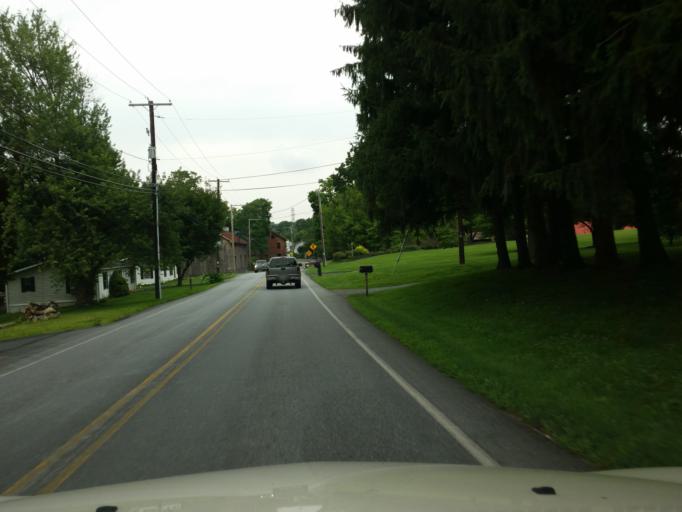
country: US
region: Pennsylvania
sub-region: Lancaster County
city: Lampeter
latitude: 40.0241
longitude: -76.2411
